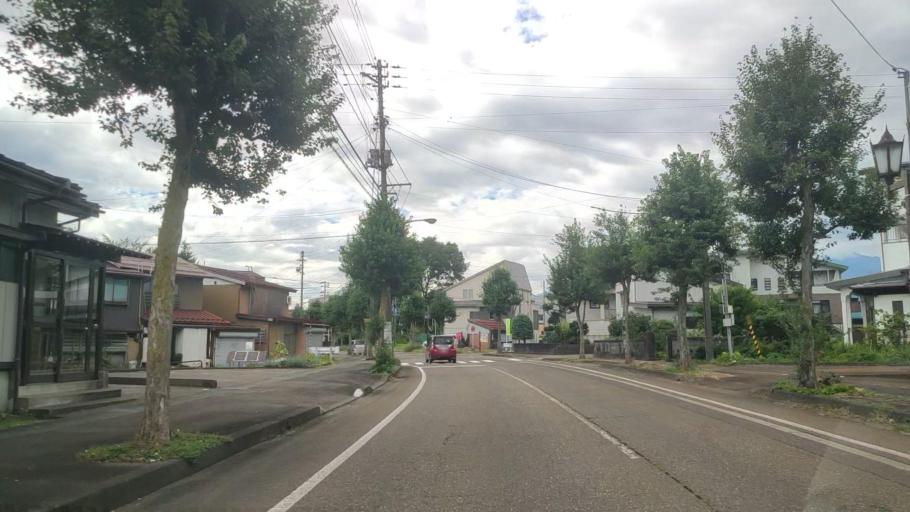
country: JP
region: Niigata
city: Arai
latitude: 37.0263
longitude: 138.2463
